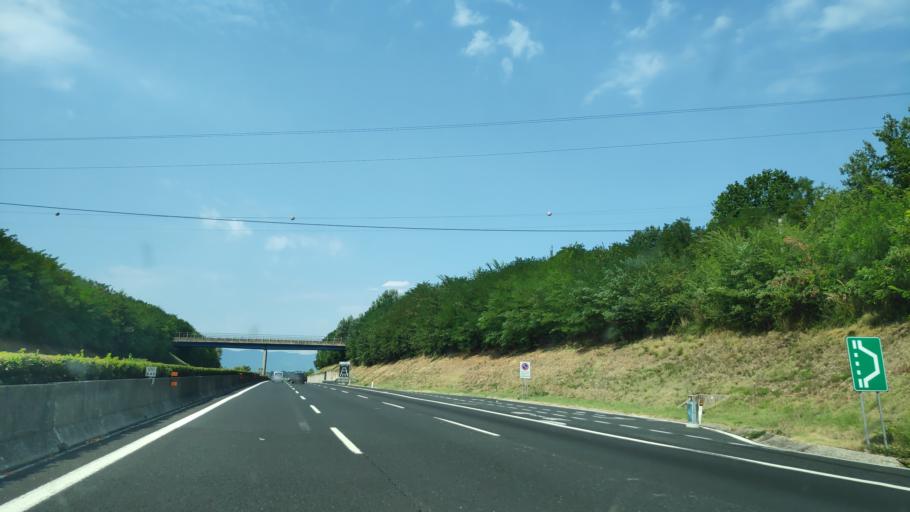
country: IT
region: Latium
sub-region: Provincia di Frosinone
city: Ceprano
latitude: 41.5436
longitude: 13.5350
